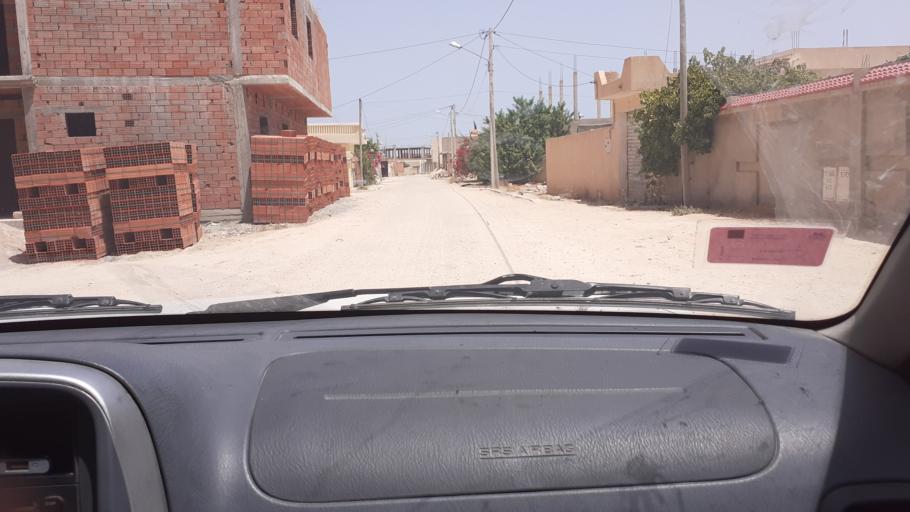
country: TN
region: Qabis
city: Matmata
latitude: 33.6111
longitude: 10.2901
